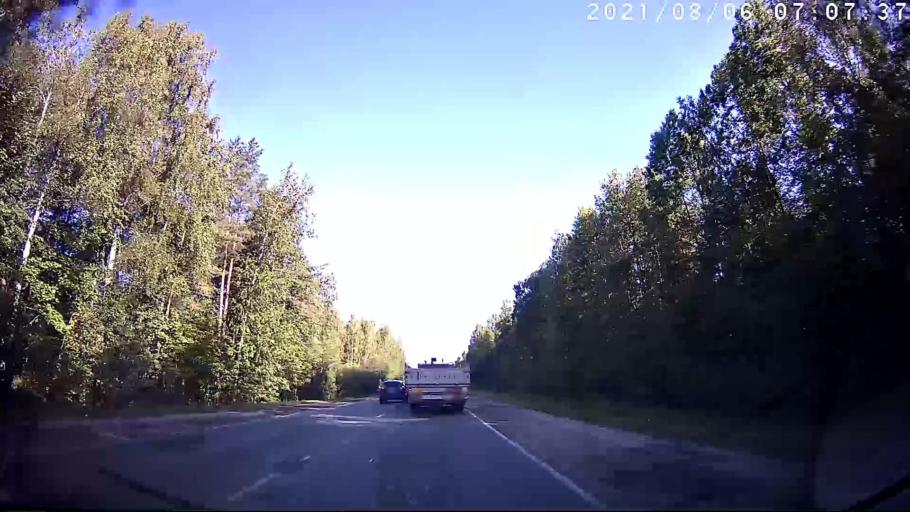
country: RU
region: Mariy-El
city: Yoshkar-Ola
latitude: 56.5644
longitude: 47.9776
